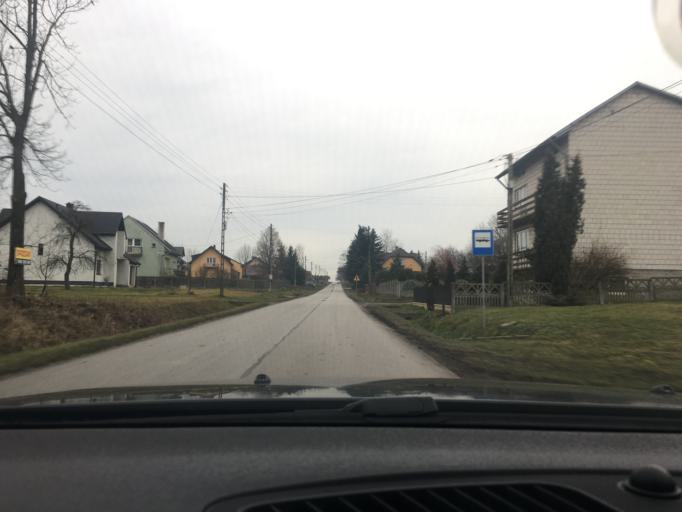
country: PL
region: Swietokrzyskie
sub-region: Powiat jedrzejowski
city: Jedrzejow
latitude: 50.6408
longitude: 20.3550
